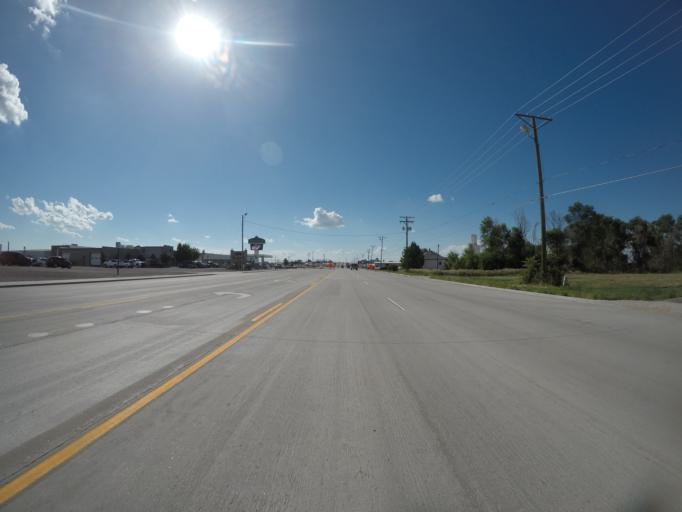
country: US
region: Colorado
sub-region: Logan County
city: Sterling
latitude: 40.6214
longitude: -103.1951
